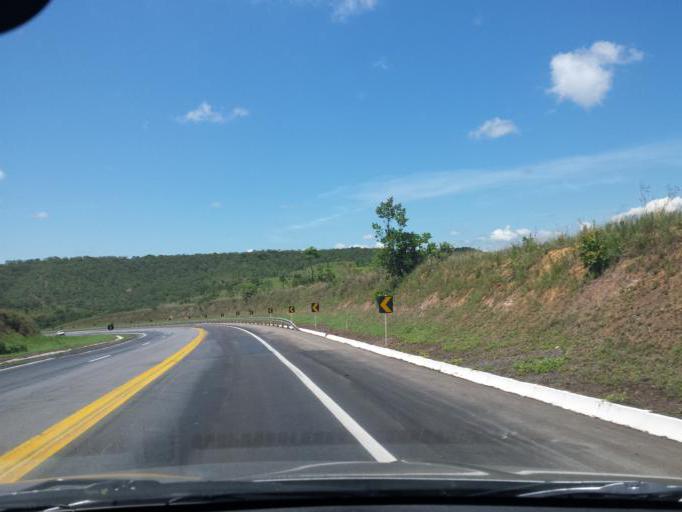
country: BR
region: Goias
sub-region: Luziania
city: Luziania
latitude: -16.3743
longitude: -47.8298
